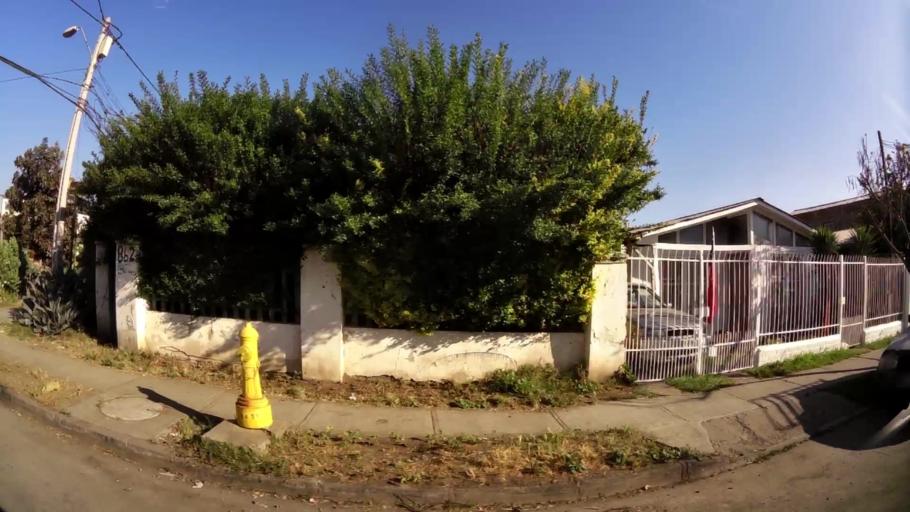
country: CL
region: Santiago Metropolitan
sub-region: Provincia de Santiago
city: Lo Prado
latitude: -33.4881
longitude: -70.7618
